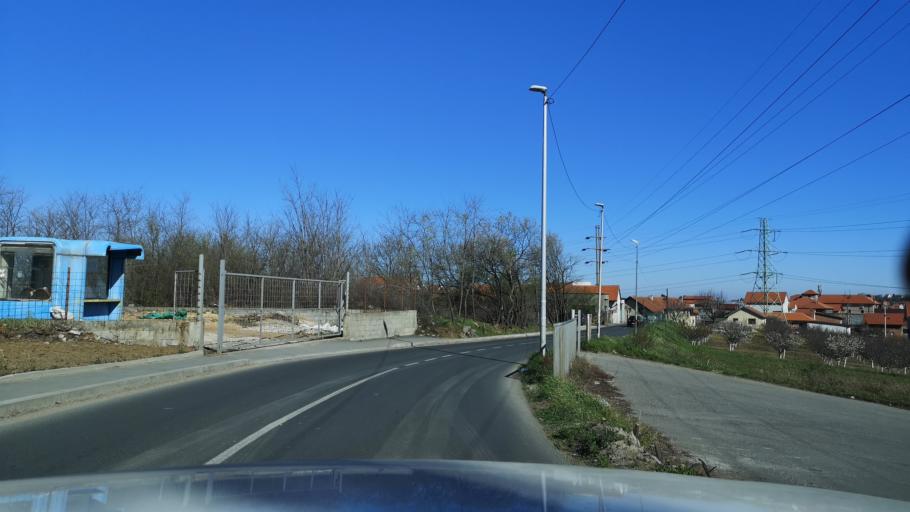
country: RS
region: Central Serbia
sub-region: Belgrade
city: Zvezdara
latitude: 44.7627
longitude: 20.5340
